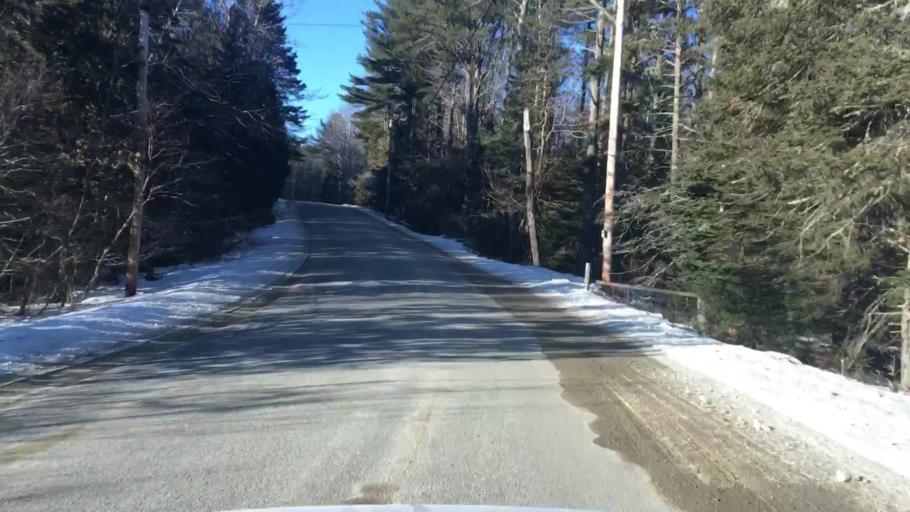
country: US
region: Maine
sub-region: Hancock County
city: Castine
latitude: 44.3393
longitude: -68.7823
